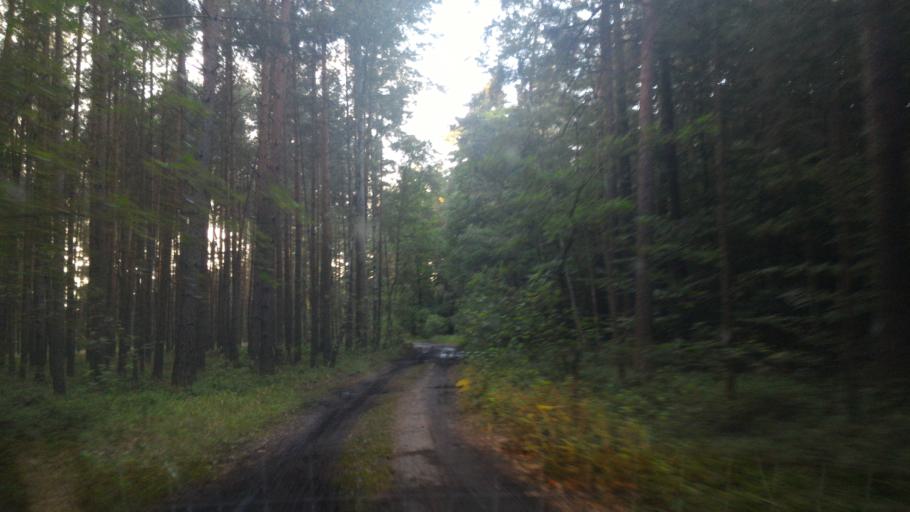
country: DE
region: Saxony
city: Horka
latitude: 51.2796
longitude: 14.9245
